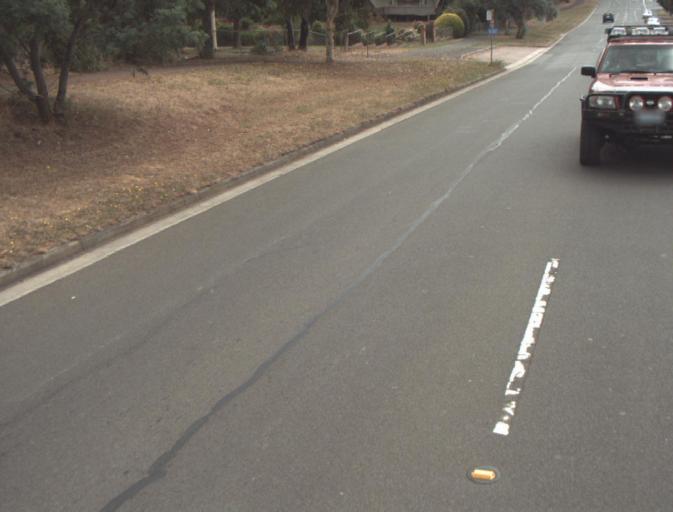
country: AU
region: Tasmania
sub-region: Launceston
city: Newstead
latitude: -41.4722
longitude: 147.1710
